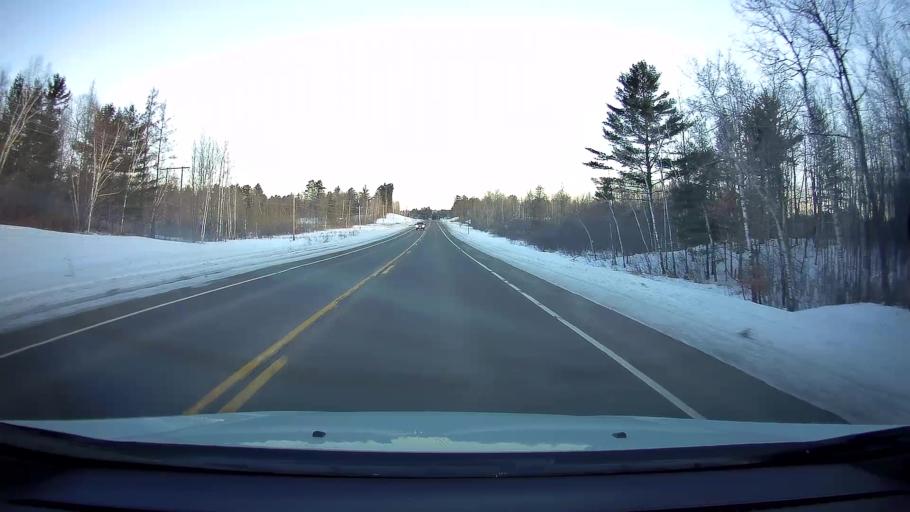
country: US
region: Wisconsin
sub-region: Barron County
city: Cumberland
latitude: 45.5921
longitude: -92.0177
